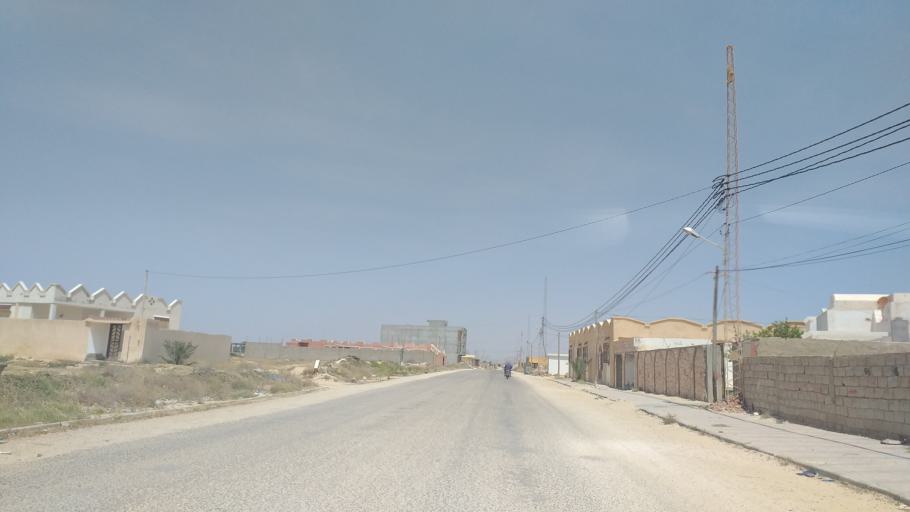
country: TN
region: Qabis
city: Gabes
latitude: 33.9526
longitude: 10.0677
